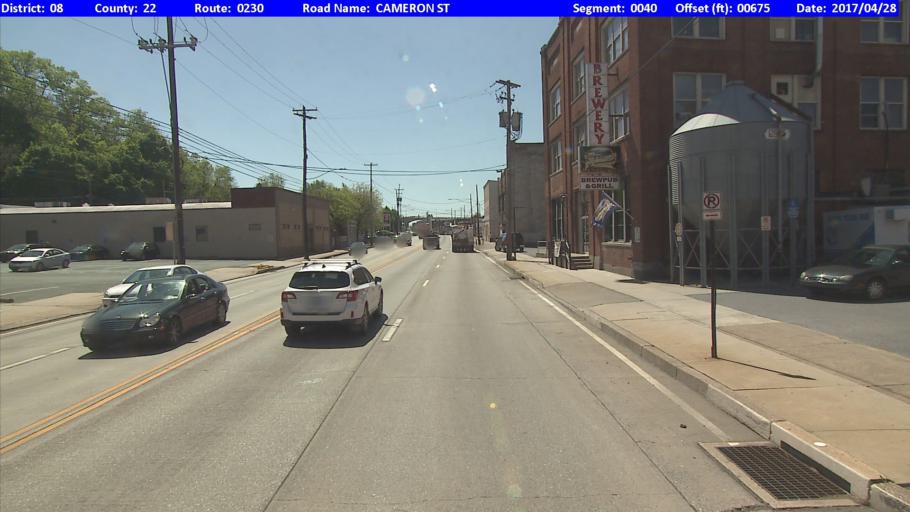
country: US
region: Pennsylvania
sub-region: Dauphin County
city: Harrisburg
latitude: 40.2662
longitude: -76.8752
